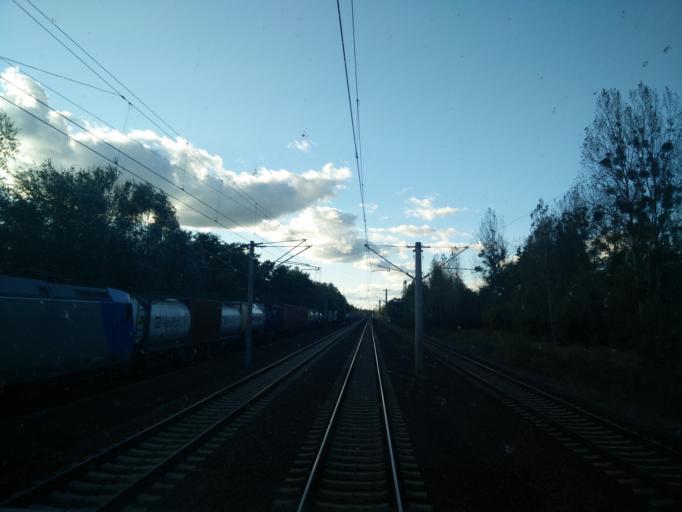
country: DE
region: Brandenburg
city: Brieselang
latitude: 52.5833
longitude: 12.9986
